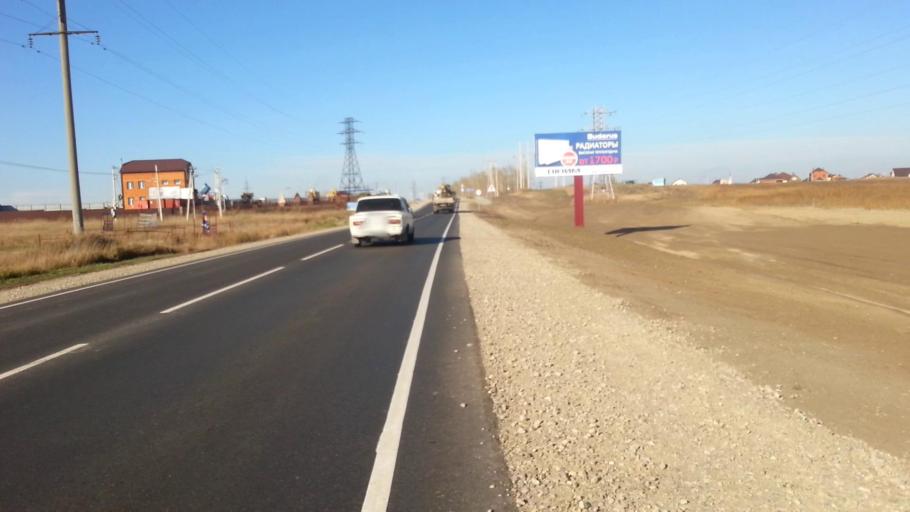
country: RU
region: Altai Krai
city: Sannikovo
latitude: 53.3341
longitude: 83.9381
